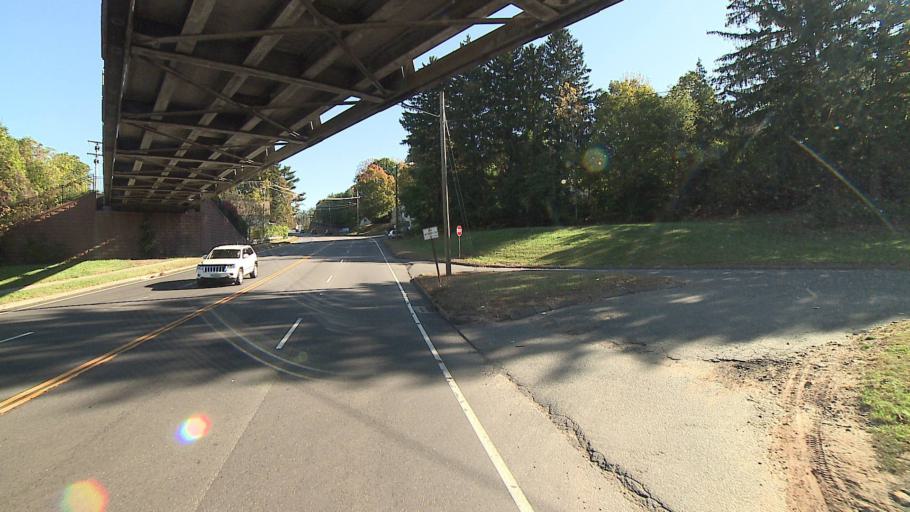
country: US
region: Connecticut
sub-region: Middlesex County
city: Middletown
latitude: 41.5565
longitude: -72.6676
